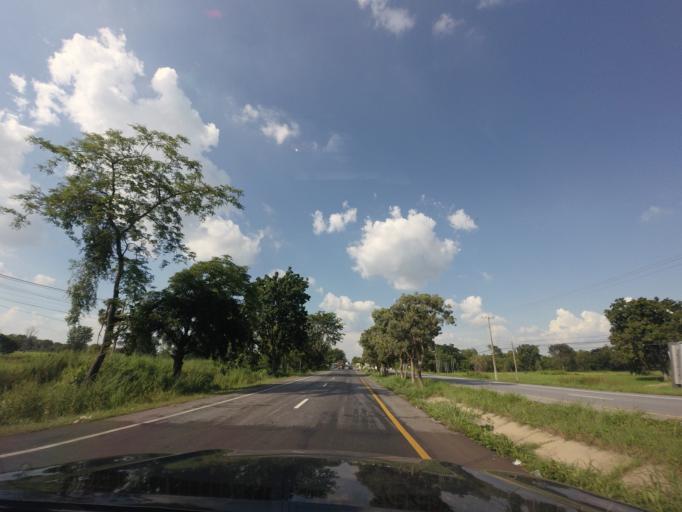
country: TH
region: Nakhon Ratchasima
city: Bua Lai
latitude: 15.7087
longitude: 102.5871
